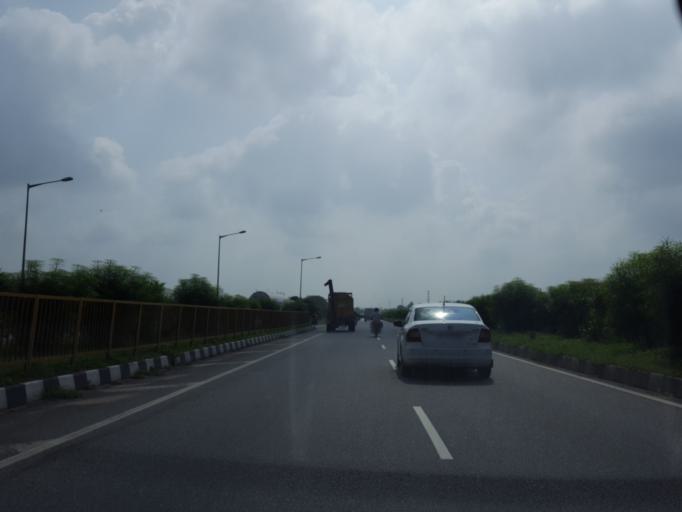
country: IN
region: Telangana
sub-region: Nalgonda
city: Gudur
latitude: 17.2730
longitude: 78.8175
